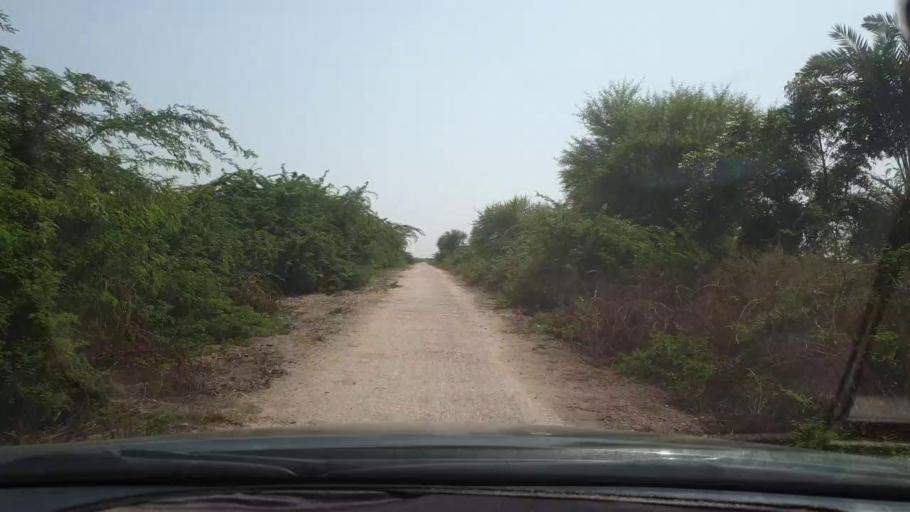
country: PK
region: Sindh
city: Naukot
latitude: 24.8113
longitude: 69.2442
